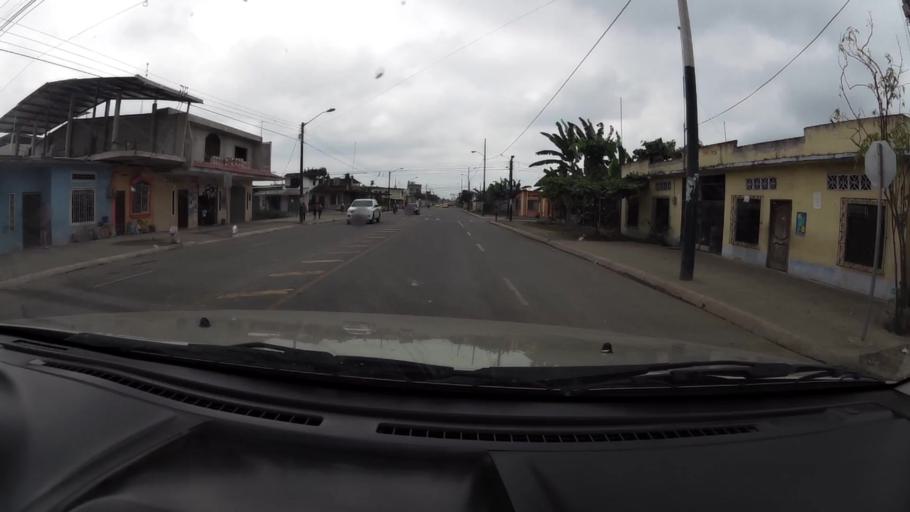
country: EC
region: El Oro
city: Pasaje
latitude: -3.2410
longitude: -79.8326
